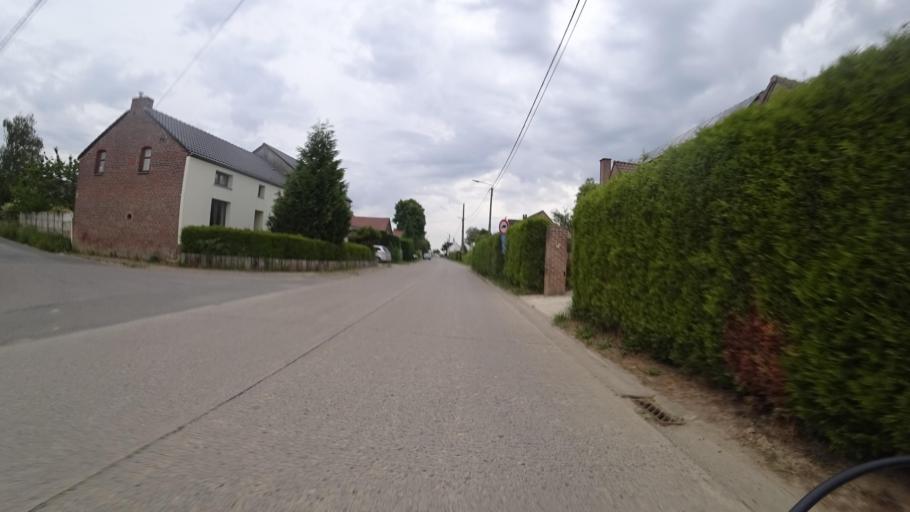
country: BE
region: Wallonia
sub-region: Province de Namur
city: Gembloux
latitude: 50.5700
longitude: 4.7683
